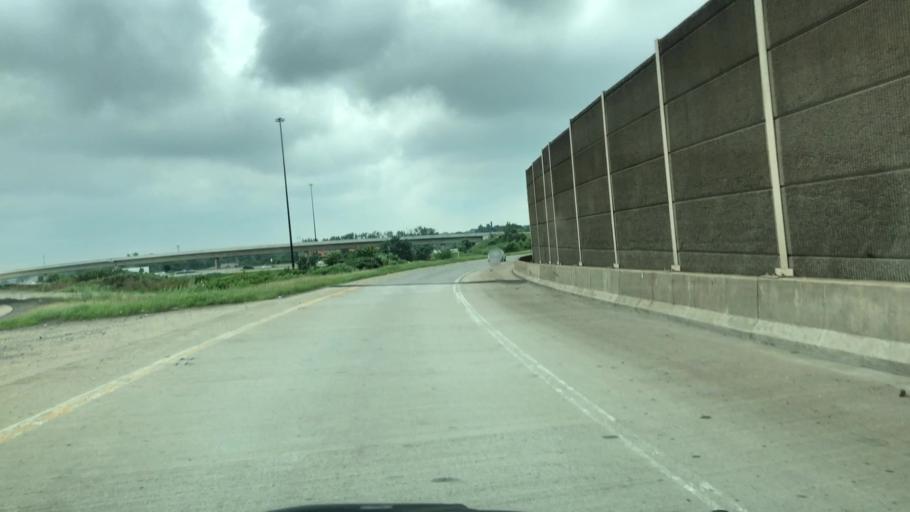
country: US
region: Indiana
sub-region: Lake County
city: Highland
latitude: 41.5736
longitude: -87.4332
